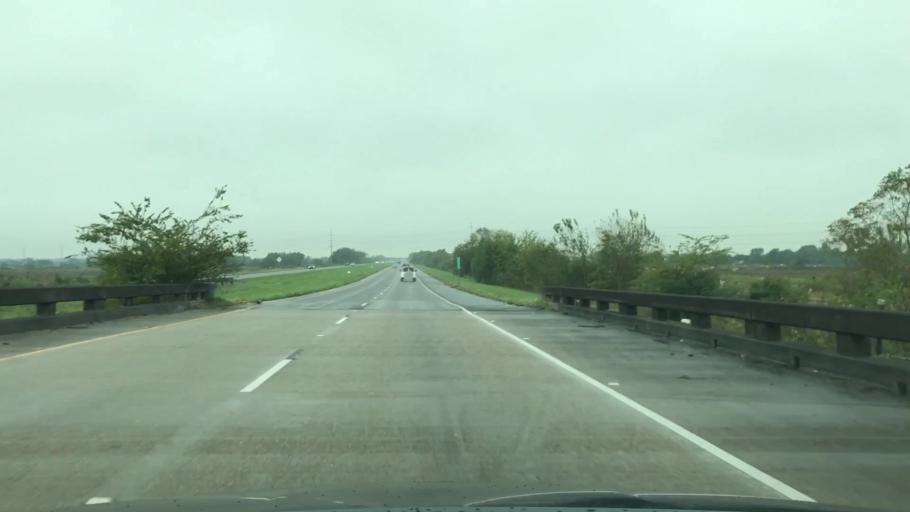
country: US
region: Louisiana
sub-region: Lafourche Parish
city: Raceland
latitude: 29.6902
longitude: -90.6057
